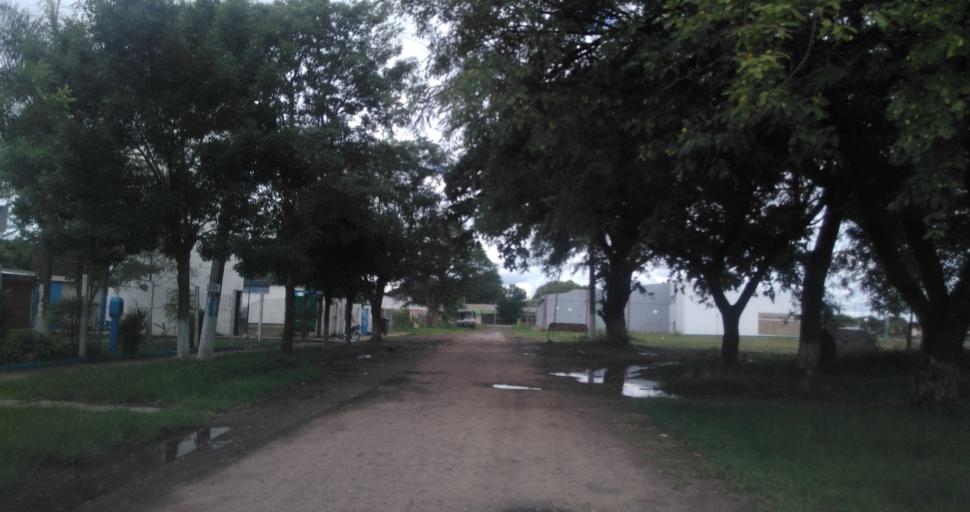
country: AR
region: Chaco
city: Fontana
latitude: -27.4191
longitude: -59.0362
